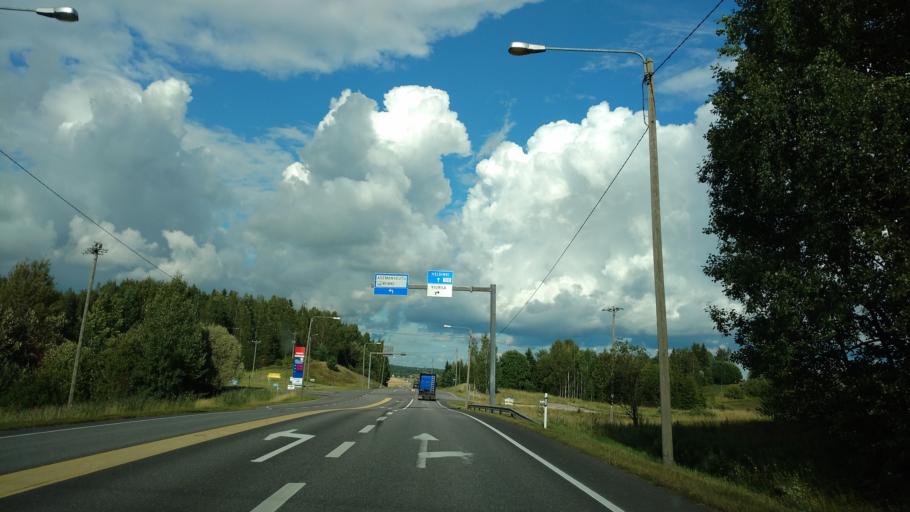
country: FI
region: Varsinais-Suomi
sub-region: Salo
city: Halikko
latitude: 60.3827
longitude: 23.0402
